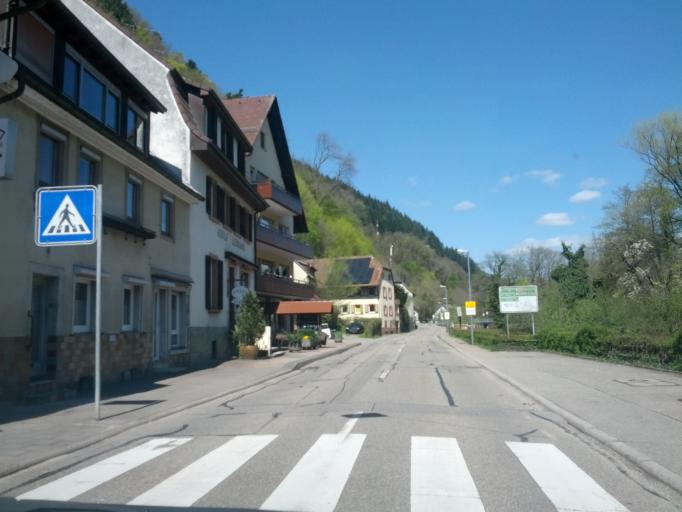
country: DE
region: Baden-Wuerttemberg
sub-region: Freiburg Region
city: Gutach im Breisgau
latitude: 48.1150
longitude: 7.9853
